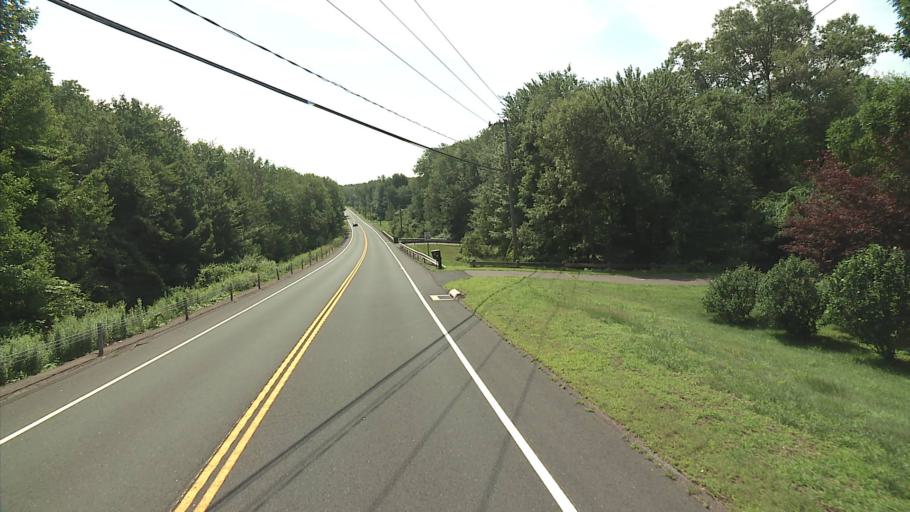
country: US
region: Connecticut
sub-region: Tolland County
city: Tolland
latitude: 41.8361
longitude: -72.4055
